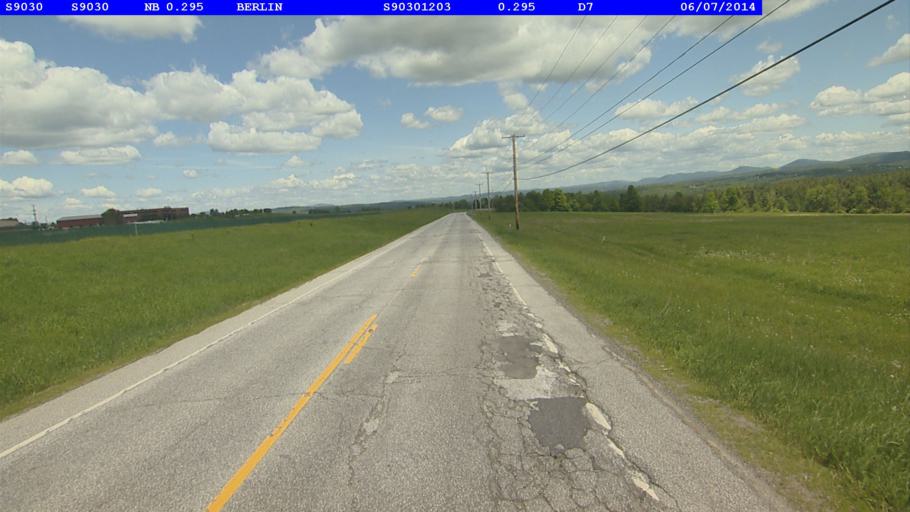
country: US
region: Vermont
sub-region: Washington County
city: Montpelier
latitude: 44.2072
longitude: -72.5598
